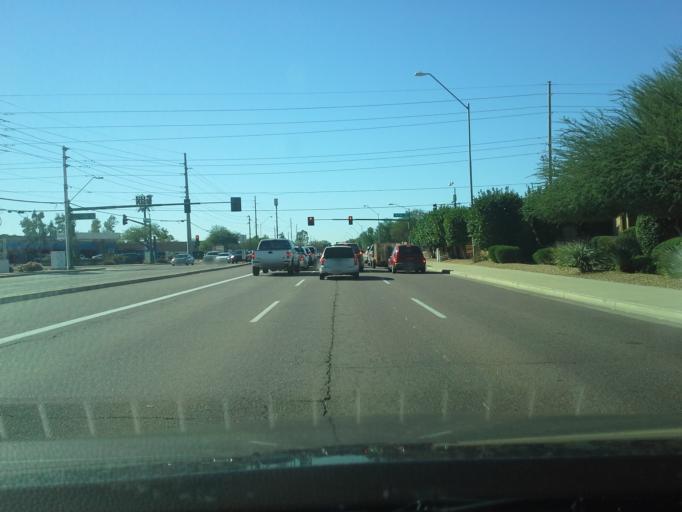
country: US
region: Arizona
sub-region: Maricopa County
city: Paradise Valley
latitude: 33.6405
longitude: -111.9591
